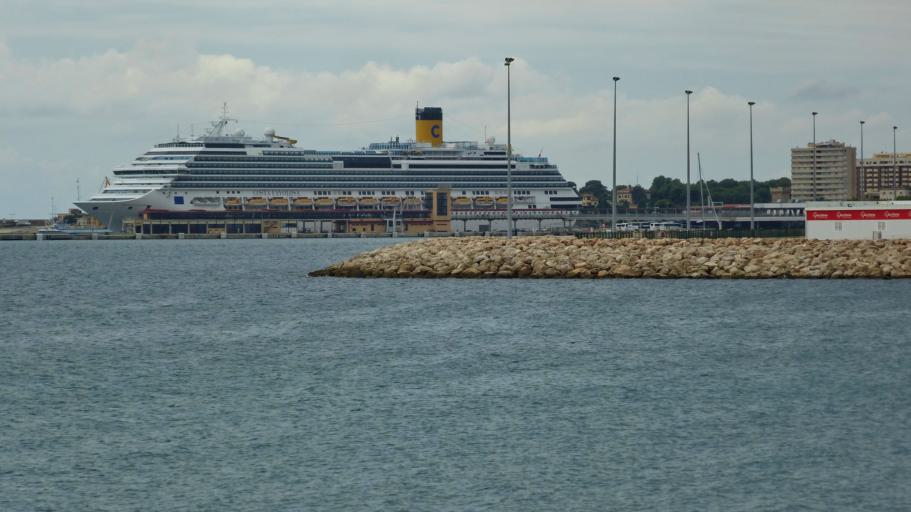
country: ES
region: Balearic Islands
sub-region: Illes Balears
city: Palma
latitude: 39.5660
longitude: 2.6454
